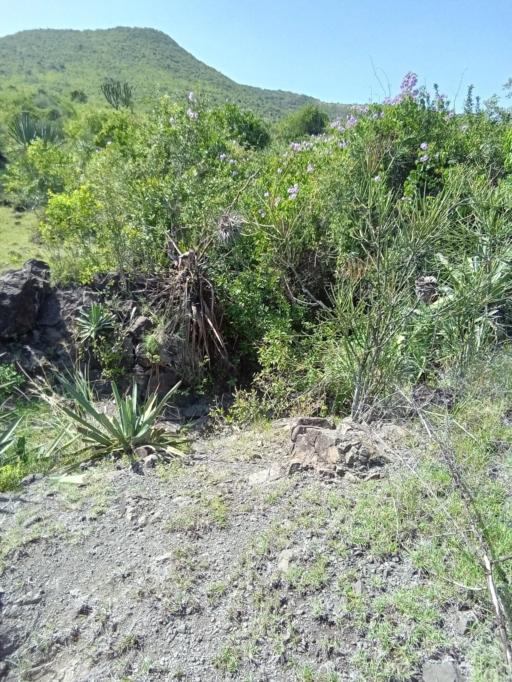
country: KE
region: Homa Bay
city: Homa Bay
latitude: -0.4715
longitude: 34.1897
